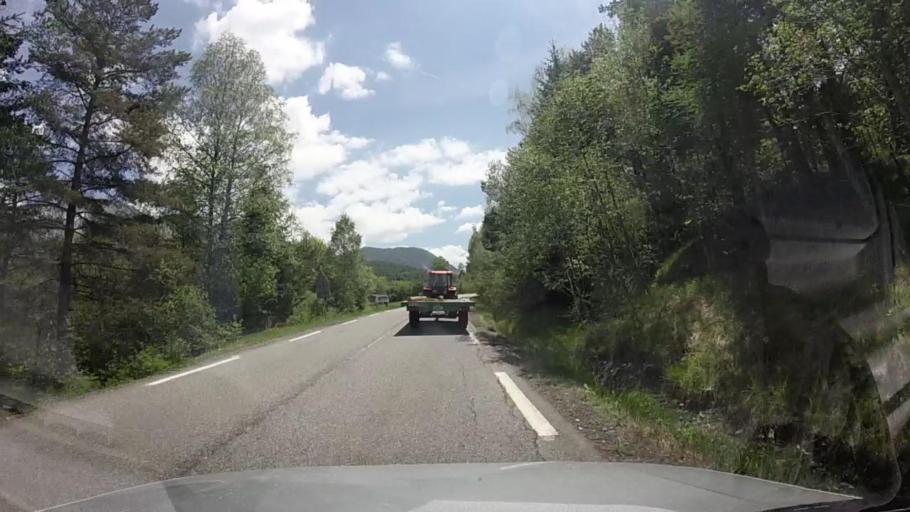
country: FR
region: Provence-Alpes-Cote d'Azur
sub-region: Departement des Alpes-de-Haute-Provence
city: Seyne-les-Alpes
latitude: 44.3239
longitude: 6.3975
